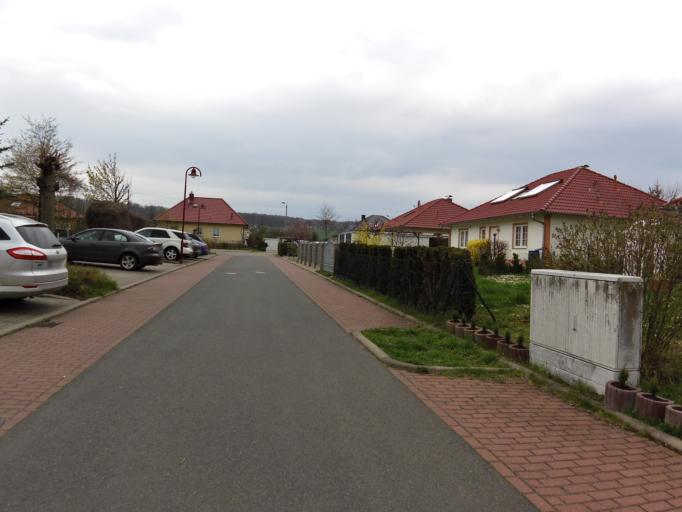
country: DE
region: Thuringia
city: Gotha
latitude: 50.9606
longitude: 10.6936
